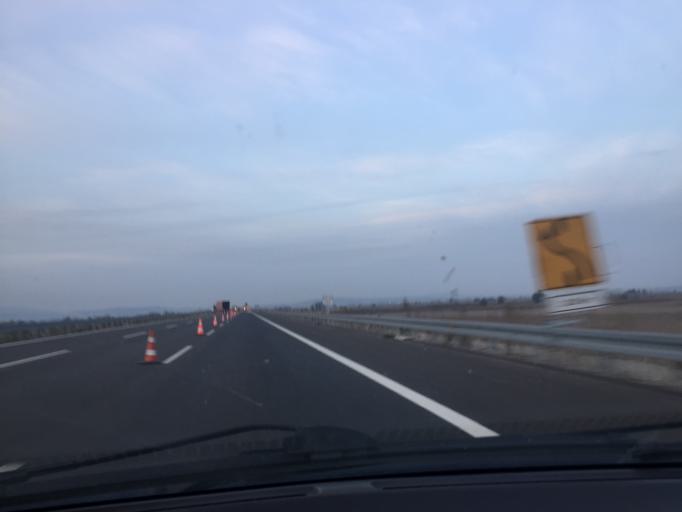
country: TR
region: Manisa
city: Halitpasa
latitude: 38.7205
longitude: 27.6516
